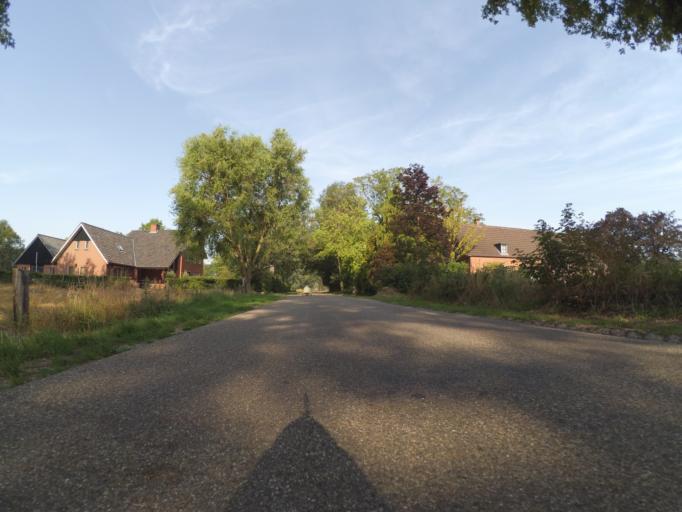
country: NL
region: Overijssel
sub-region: Gemeente Borne
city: Borne
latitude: 52.3389
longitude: 6.7880
